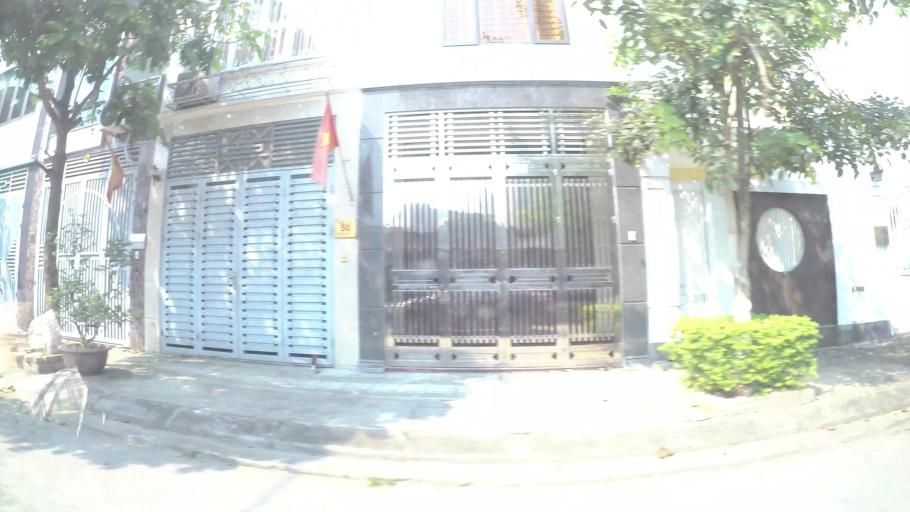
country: VN
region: Ha Noi
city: Ha Dong
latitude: 20.9556
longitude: 105.8054
